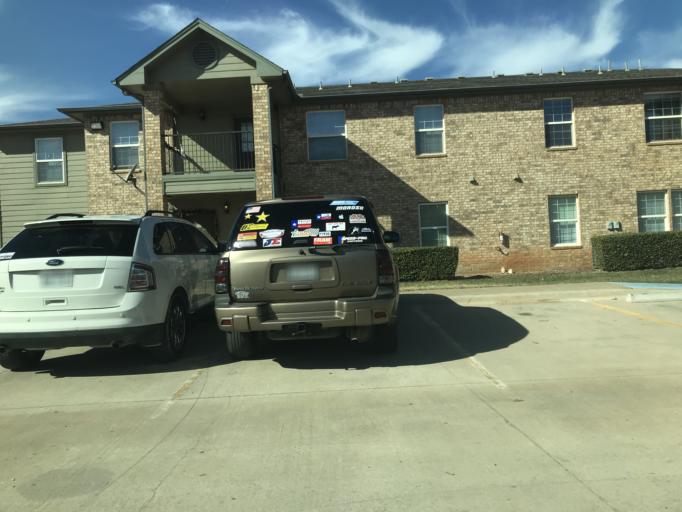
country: US
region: Texas
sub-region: Taylor County
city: Abilene
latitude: 32.4863
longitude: -99.7473
